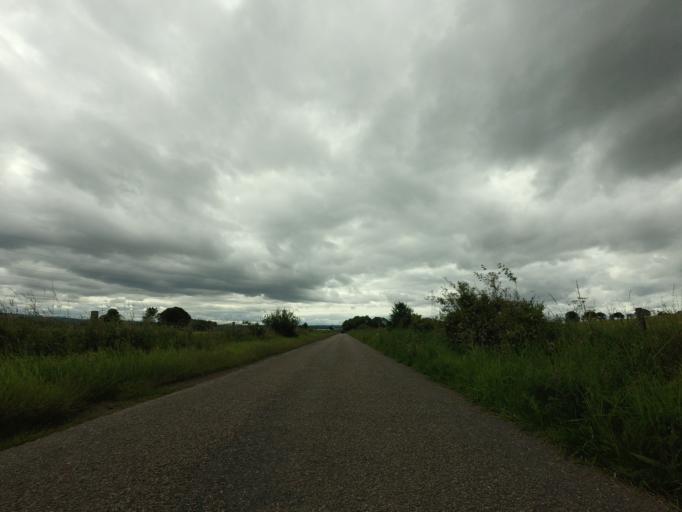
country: GB
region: Scotland
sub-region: Moray
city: Forres
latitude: 57.6131
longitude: -3.6850
